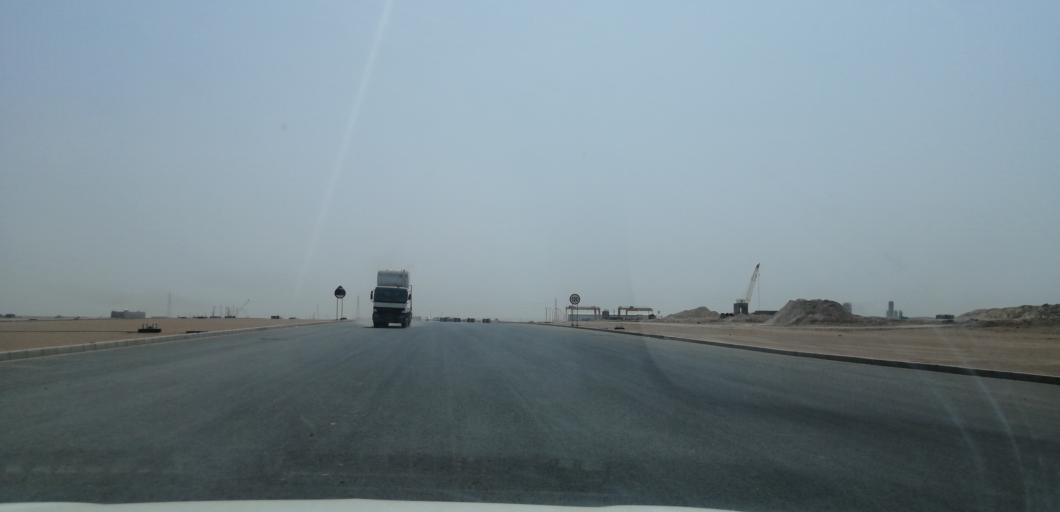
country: KW
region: Muhafazat al Jahra'
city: Al Jahra'
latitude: 29.4467
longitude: 47.6237
